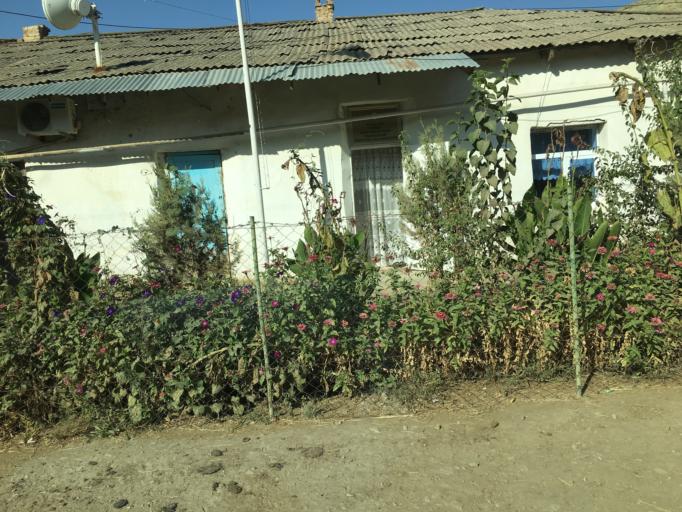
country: TM
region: Balkan
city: Magtymguly
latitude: 38.3004
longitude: 56.7437
